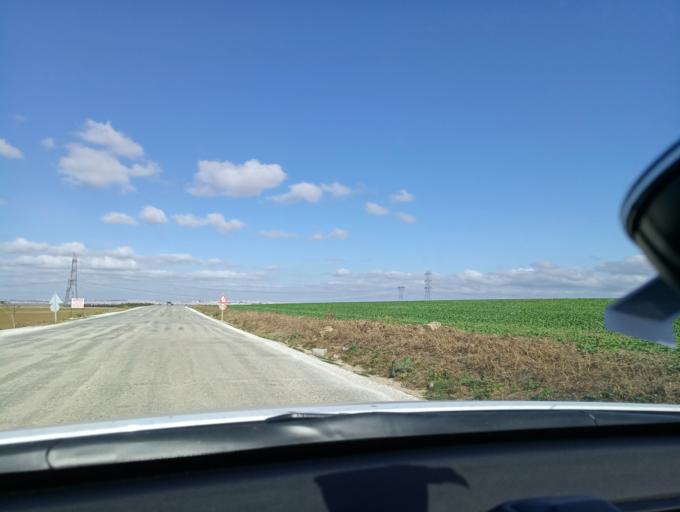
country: TR
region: Tekirdag
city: Corlu
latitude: 41.0558
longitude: 27.8349
